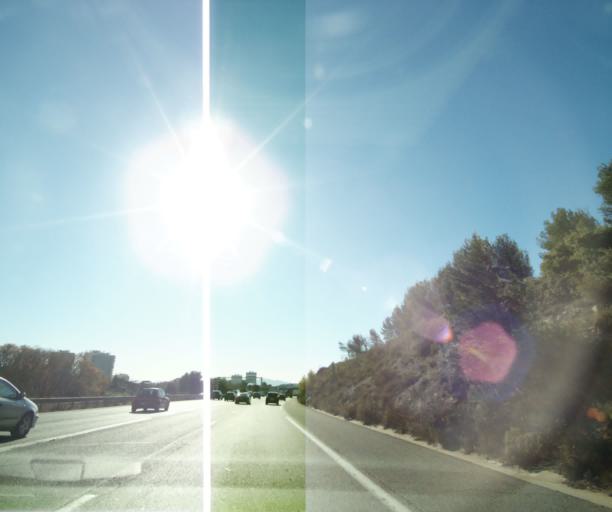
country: FR
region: Provence-Alpes-Cote d'Azur
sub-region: Departement des Bouches-du-Rhone
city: Septemes-les-Vallons
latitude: 43.3935
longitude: 5.3510
